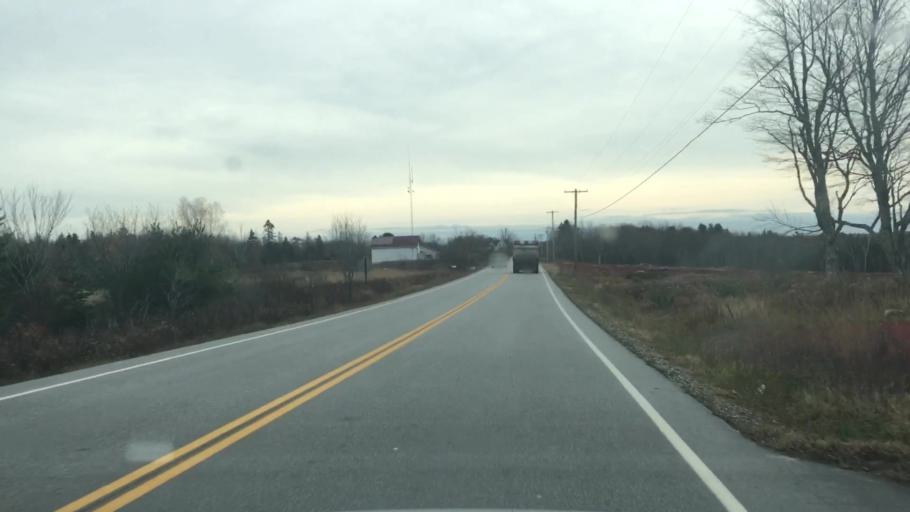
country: US
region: Maine
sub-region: Hancock County
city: Penobscot
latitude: 44.5262
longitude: -68.6655
